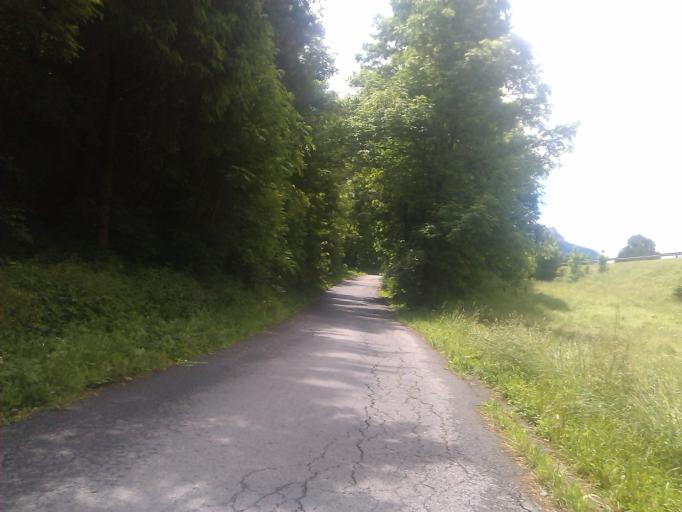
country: AT
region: Tyrol
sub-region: Politischer Bezirk Landeck
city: Fiss
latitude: 47.0324
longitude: 10.6307
